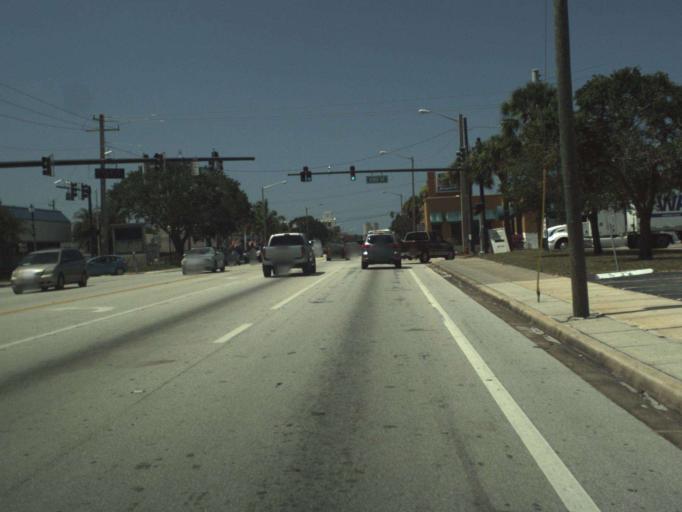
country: US
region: Florida
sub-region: Saint Lucie County
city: Fort Pierce
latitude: 27.4391
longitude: -80.3258
